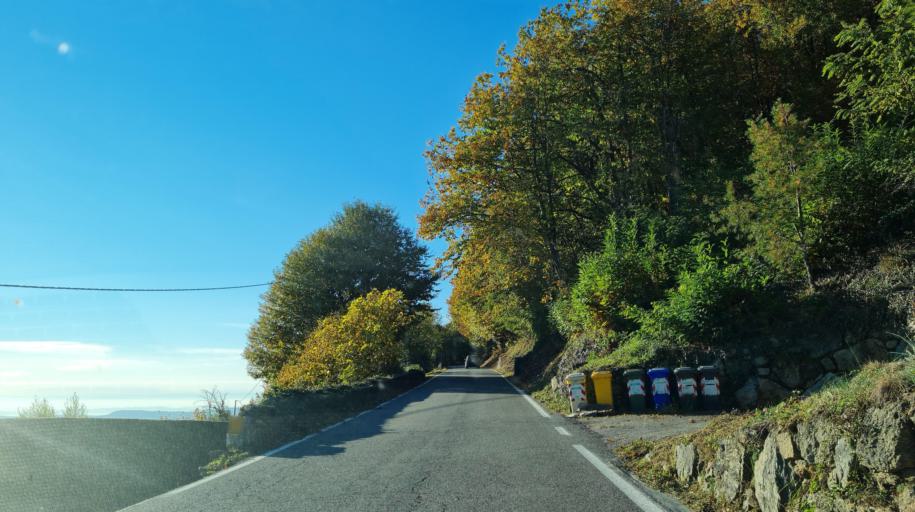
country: IT
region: Piedmont
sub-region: Provincia di Torino
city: Lessolo
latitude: 45.4629
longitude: 7.8049
